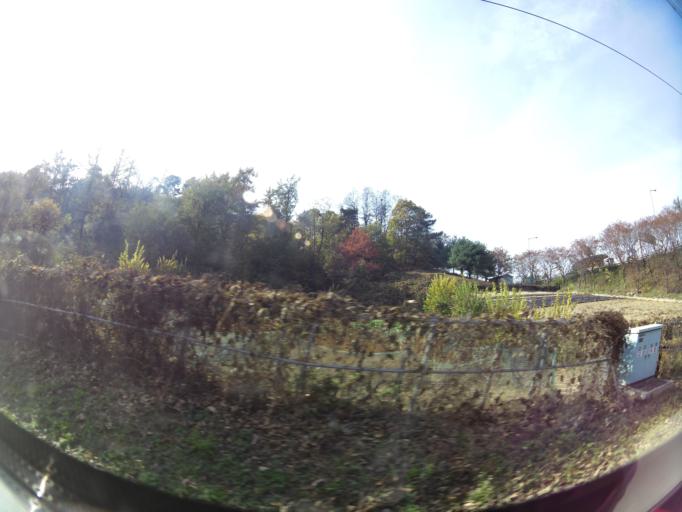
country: KR
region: Daejeon
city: Sintansin
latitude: 36.4668
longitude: 127.4215
